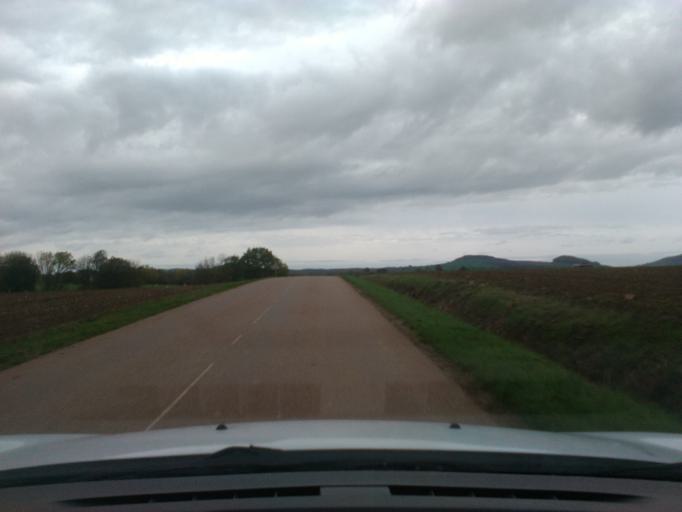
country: FR
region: Lorraine
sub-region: Departement des Vosges
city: Mirecourt
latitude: 48.3446
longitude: 6.1036
